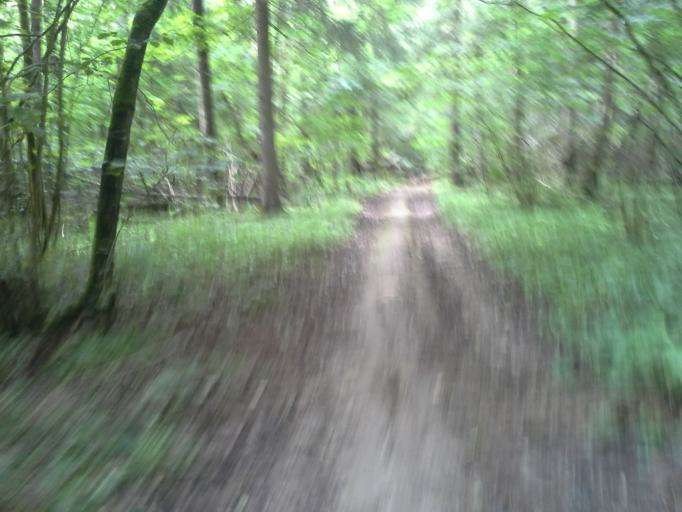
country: RU
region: Moskovskaya
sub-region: Leninskiy Rayon
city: Vnukovo
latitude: 55.6431
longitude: 37.2895
